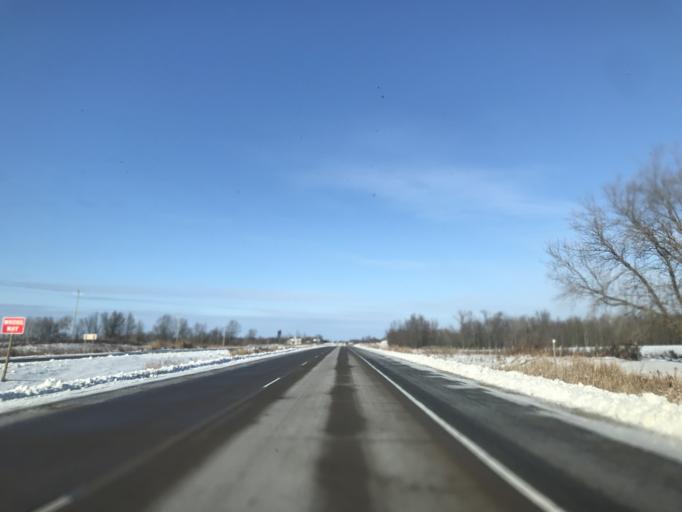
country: US
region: Wisconsin
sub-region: Oconto County
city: Oconto Falls
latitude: 44.9094
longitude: -88.0464
